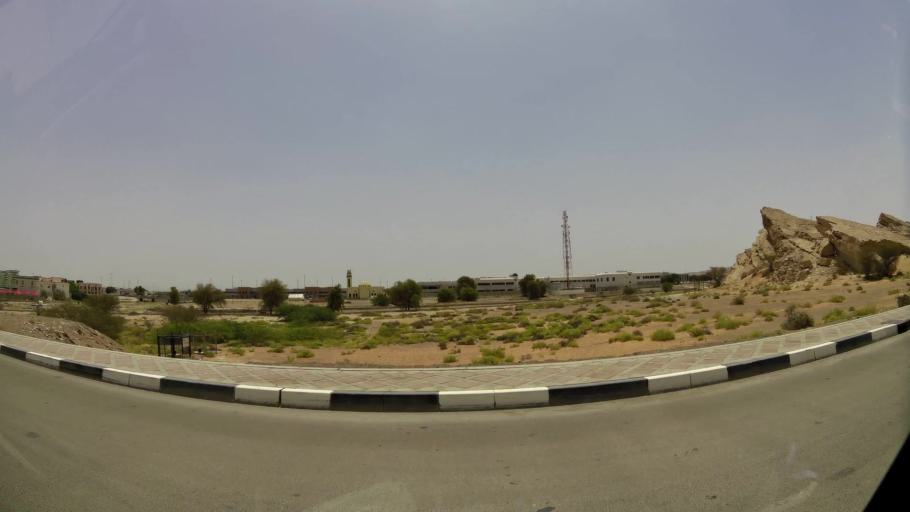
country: AE
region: Abu Dhabi
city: Al Ain
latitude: 24.2014
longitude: 55.7438
